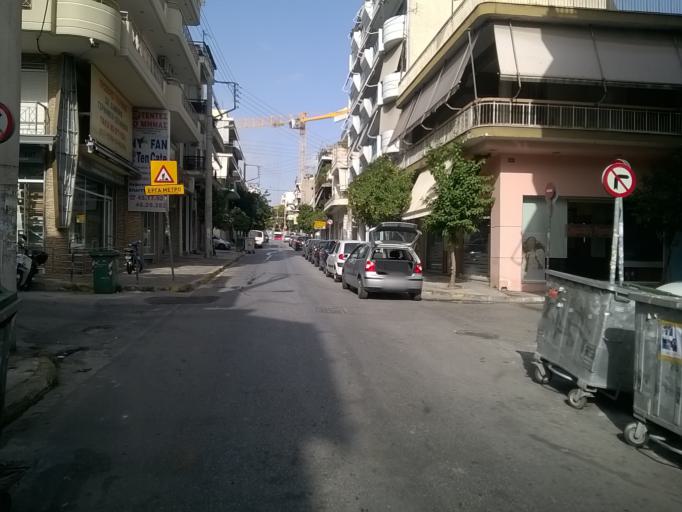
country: GR
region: Attica
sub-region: Nomos Attikis
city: Piraeus
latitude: 37.9584
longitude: 23.6398
